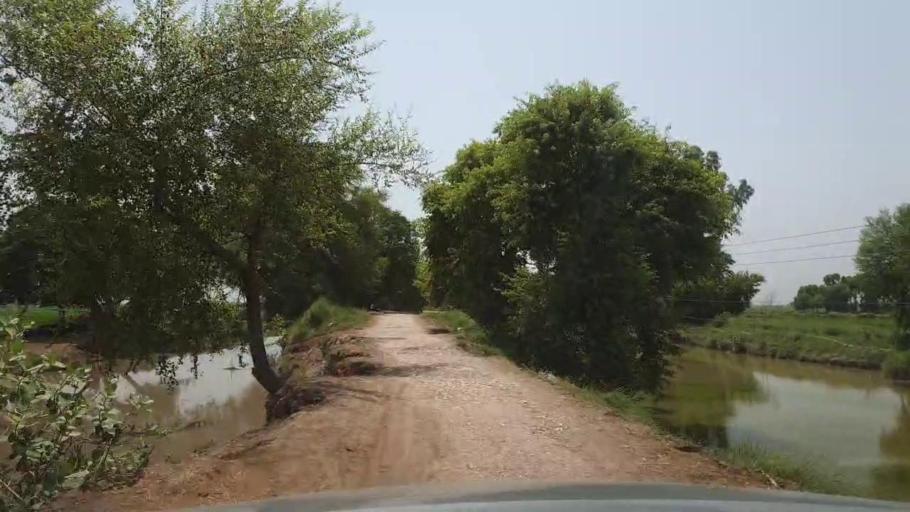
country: PK
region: Sindh
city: Ratodero
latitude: 27.7924
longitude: 68.3407
